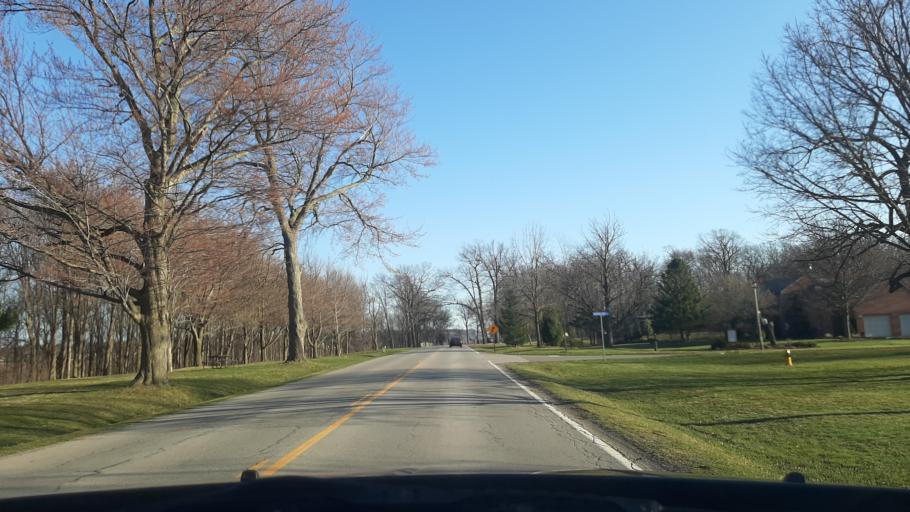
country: US
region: New York
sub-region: Niagara County
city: Lewiston
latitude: 43.1962
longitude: -79.0546
